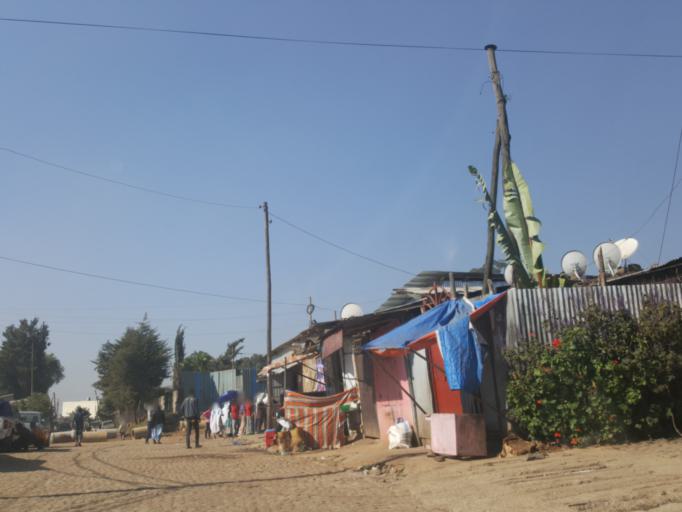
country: ET
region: Adis Abeba
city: Addis Ababa
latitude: 9.0494
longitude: 38.7331
